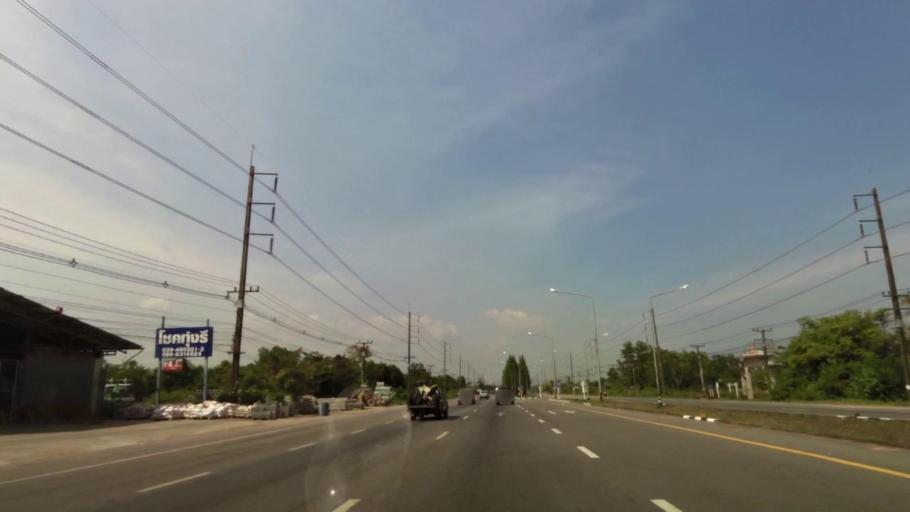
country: TH
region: Chanthaburi
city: Chanthaburi
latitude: 12.6564
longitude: 102.1247
